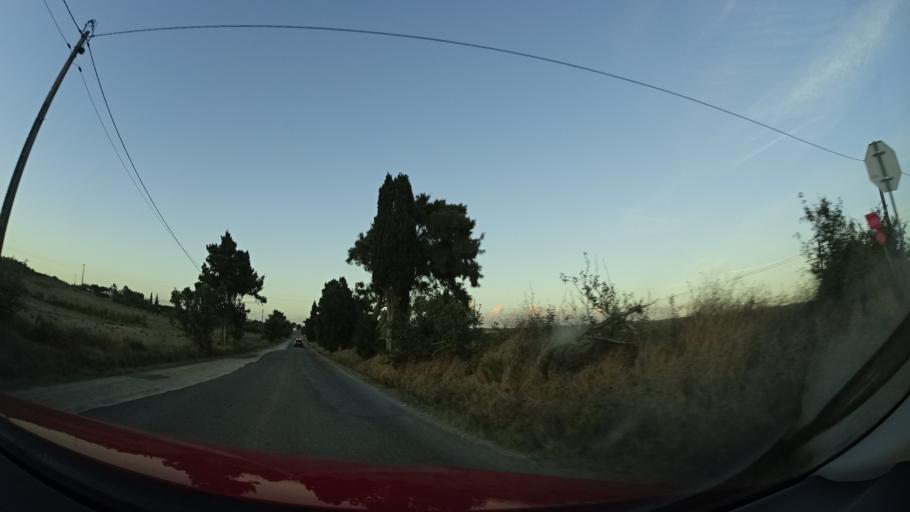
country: PT
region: Faro
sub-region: Aljezur
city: Aljezur
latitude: 37.2271
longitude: -8.8319
